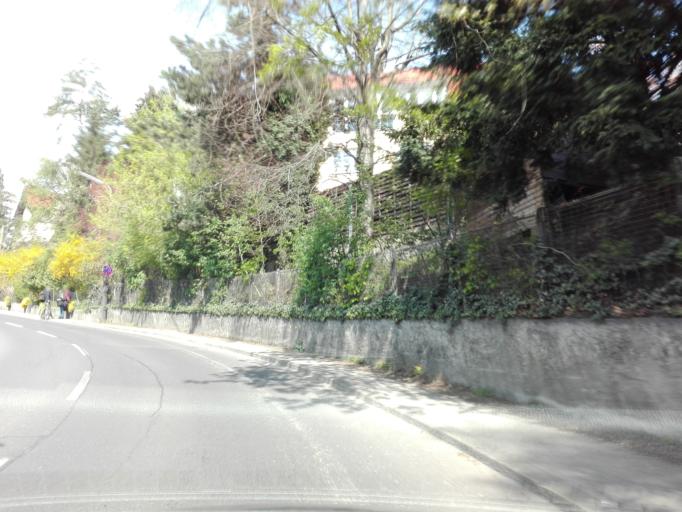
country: AT
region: Upper Austria
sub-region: Linz Stadt
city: Linz
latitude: 48.3111
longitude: 14.2729
